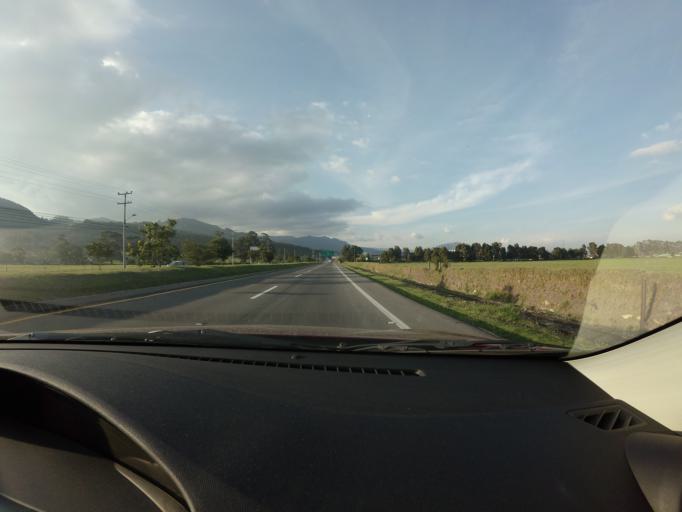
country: CO
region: Cundinamarca
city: Zipaquira
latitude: 5.0073
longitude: -74.0050
